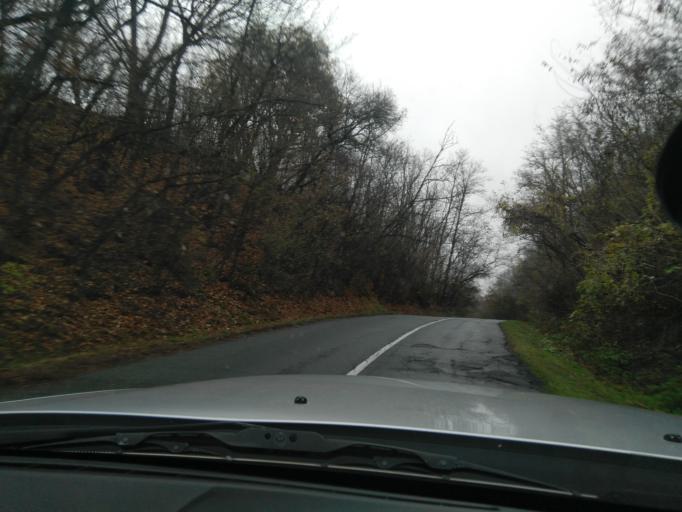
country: HU
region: Nograd
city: Kazar
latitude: 48.0447
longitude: 19.8975
